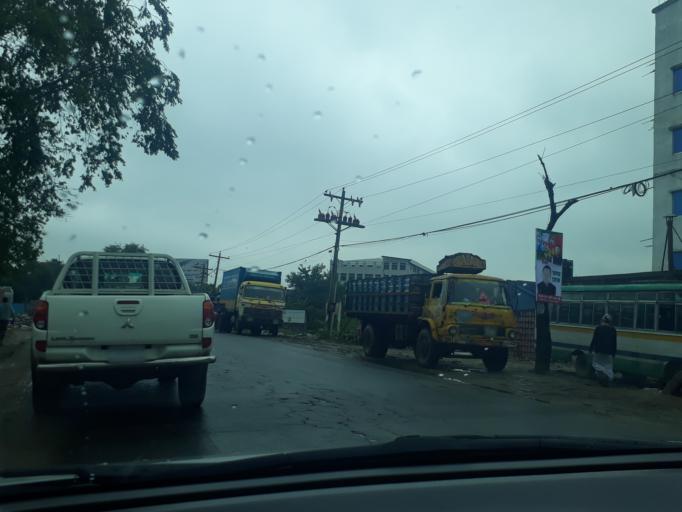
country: BD
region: Dhaka
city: Tungi
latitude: 23.9059
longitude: 90.3227
